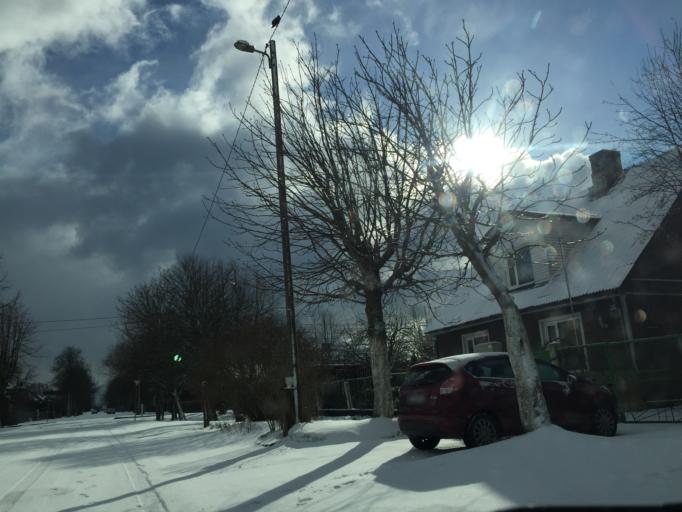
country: LV
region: Ventspils
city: Ventspils
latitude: 57.3815
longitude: 21.5618
